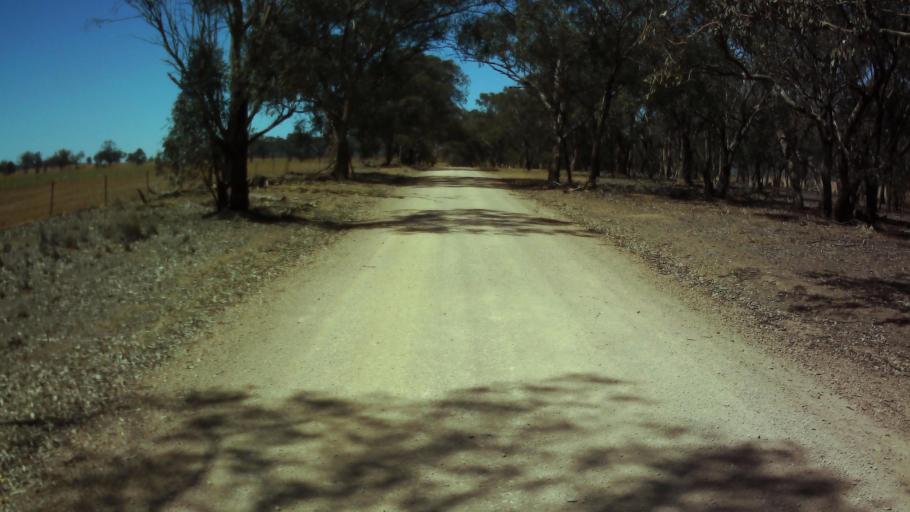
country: AU
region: New South Wales
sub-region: Weddin
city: Grenfell
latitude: -33.9269
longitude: 148.0781
